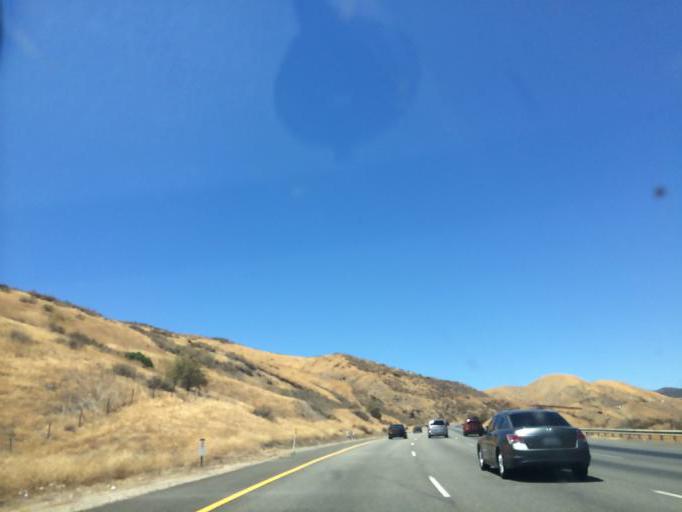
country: US
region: California
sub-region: Los Angeles County
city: Castaic
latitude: 34.5186
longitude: -118.6424
